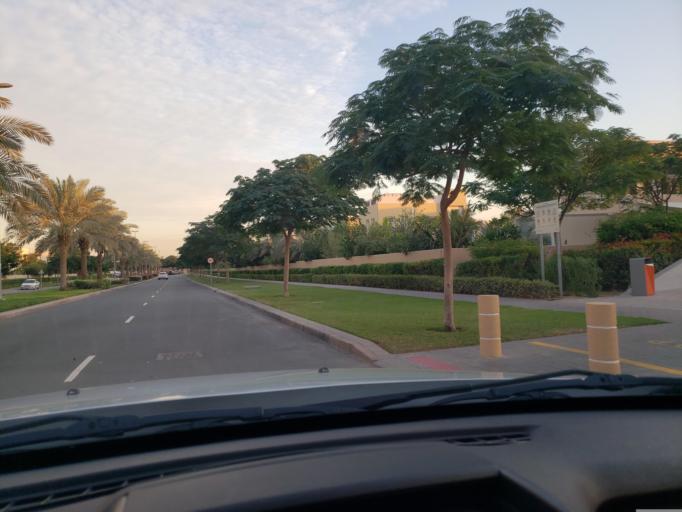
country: AE
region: Dubai
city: Dubai
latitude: 25.0264
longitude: 55.2674
